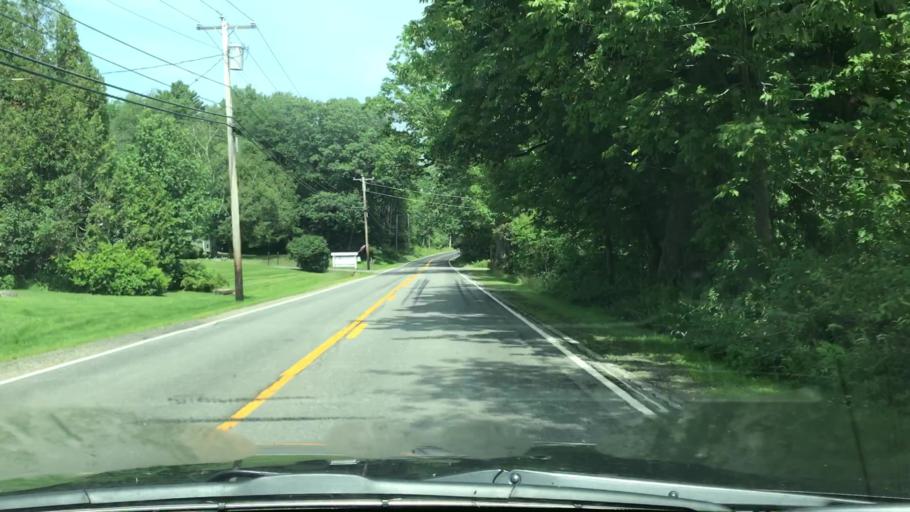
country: US
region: Maine
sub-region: Waldo County
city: Lincolnville
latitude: 44.2549
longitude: -69.0285
